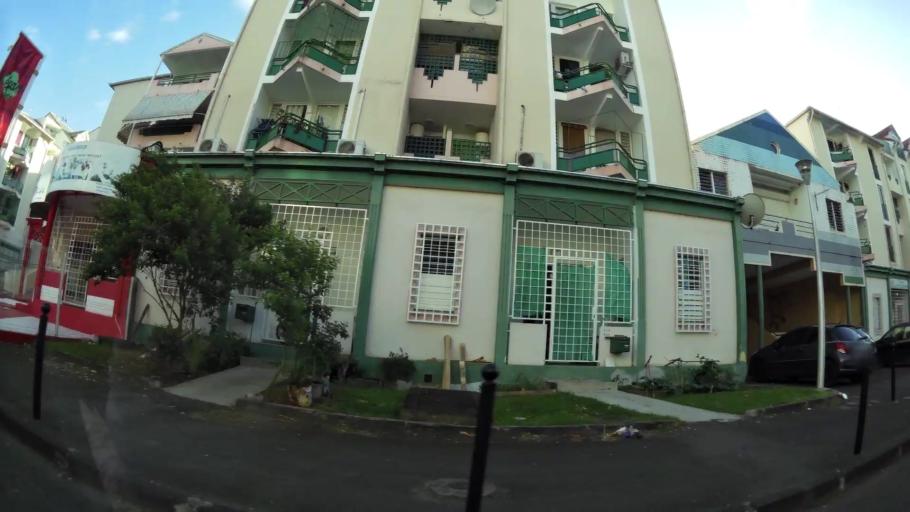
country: GP
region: Guadeloupe
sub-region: Guadeloupe
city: Pointe-a-Pitre
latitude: 16.2315
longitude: -61.5315
